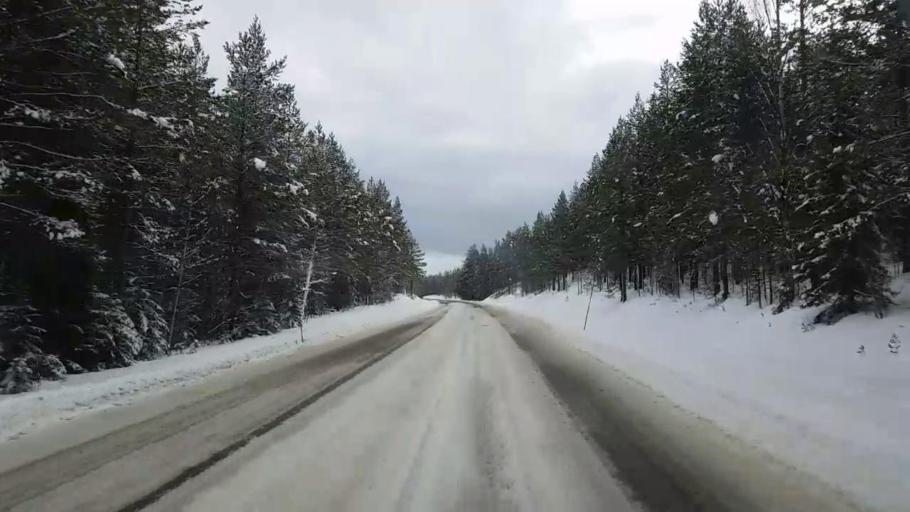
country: SE
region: Vaesternorrland
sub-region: Ange Kommun
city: Ange
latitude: 62.0730
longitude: 15.1023
